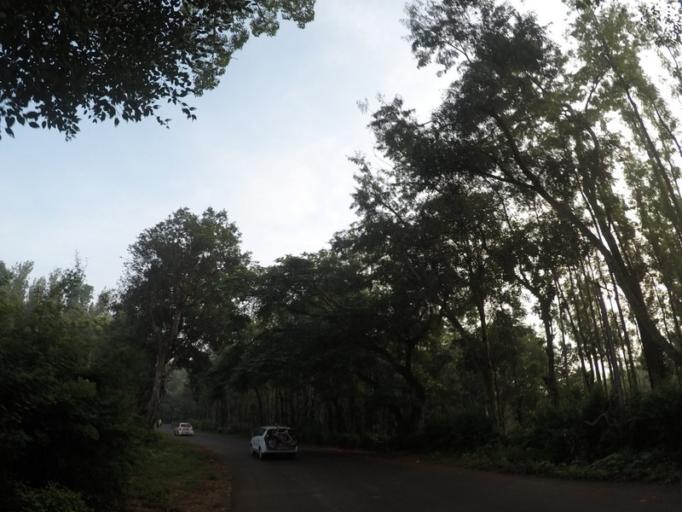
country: IN
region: Karnataka
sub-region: Chikmagalur
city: Chikmagalur
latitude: 13.4223
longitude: 75.8034
